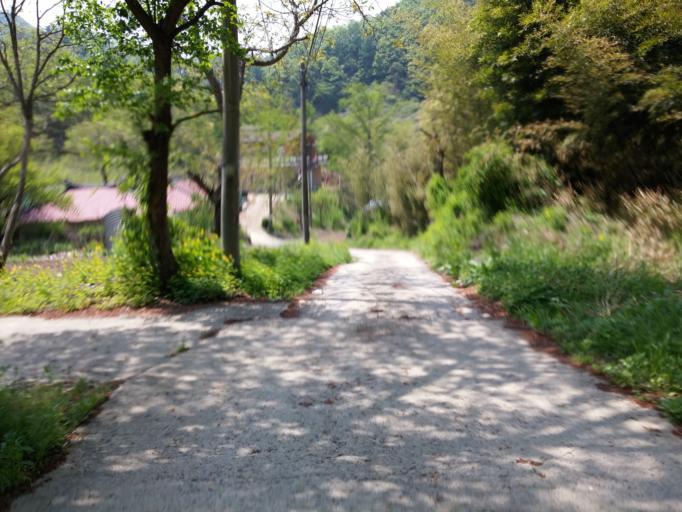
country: KR
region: Chungcheongbuk-do
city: Okcheon
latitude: 36.4139
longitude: 127.5990
